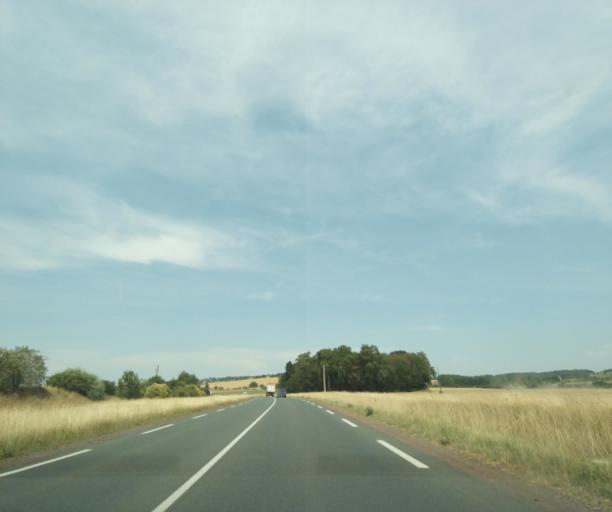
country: FR
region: Poitou-Charentes
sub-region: Departement de la Vienne
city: Chatellerault
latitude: 46.7924
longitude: 0.5571
